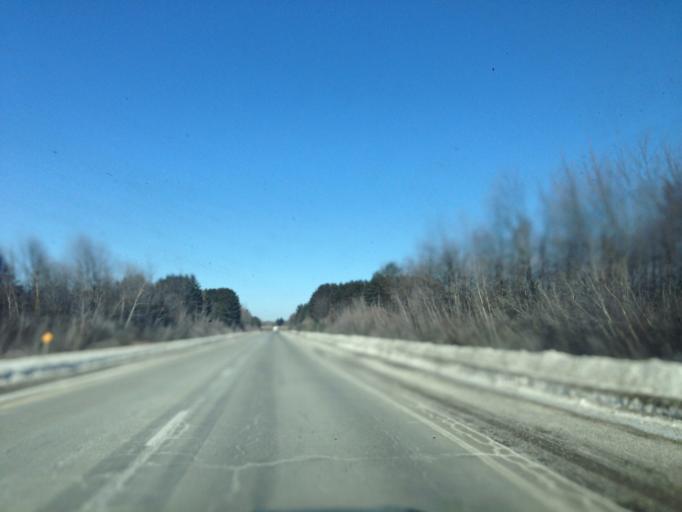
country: CA
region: Ontario
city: Ottawa
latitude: 45.3554
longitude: -75.4672
